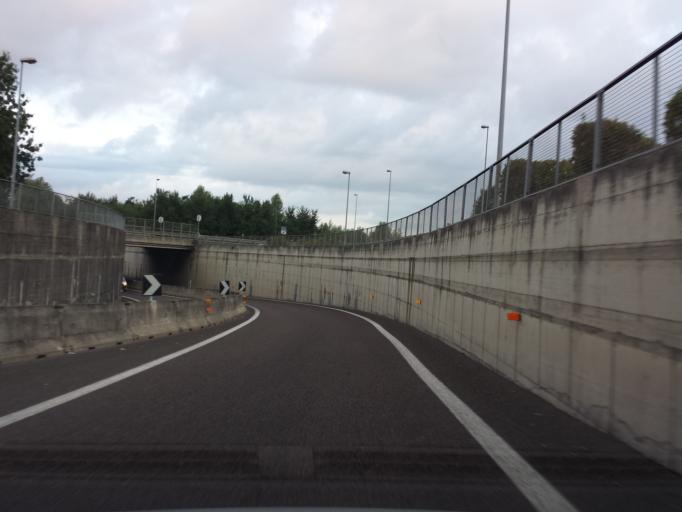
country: IT
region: Veneto
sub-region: Provincia di Padova
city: Vigodarzere
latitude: 45.4478
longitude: 11.8623
